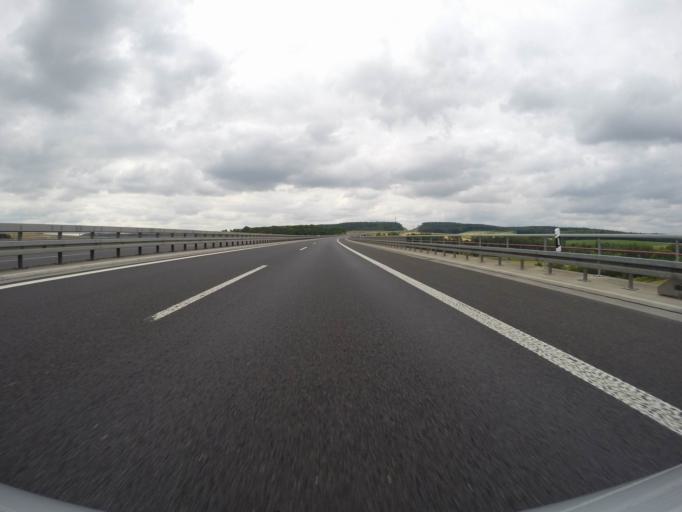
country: DE
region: Bavaria
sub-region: Regierungsbezirk Unterfranken
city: Hollstadt
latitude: 50.3458
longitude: 10.3133
